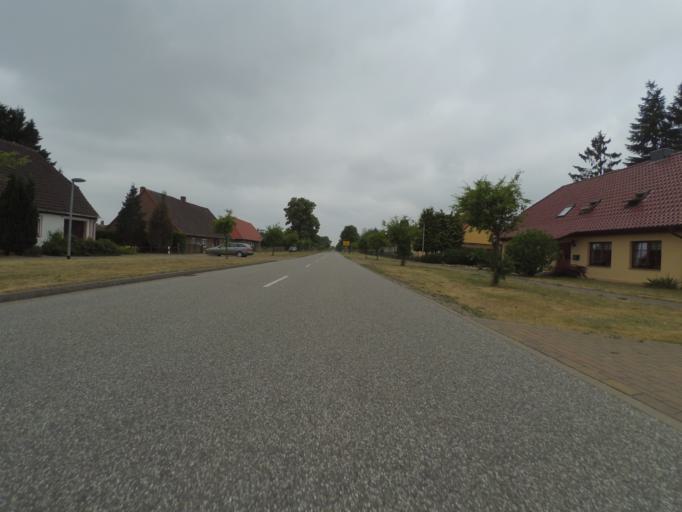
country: DE
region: Mecklenburg-Vorpommern
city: Spornitz
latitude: 53.4792
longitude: 11.6801
